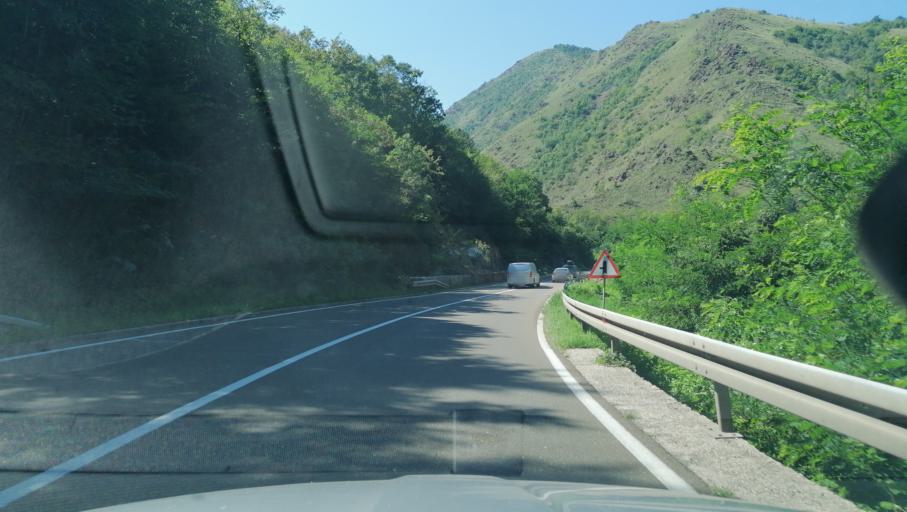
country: RS
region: Central Serbia
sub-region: Raski Okrug
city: Kraljevo
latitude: 43.5819
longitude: 20.5814
